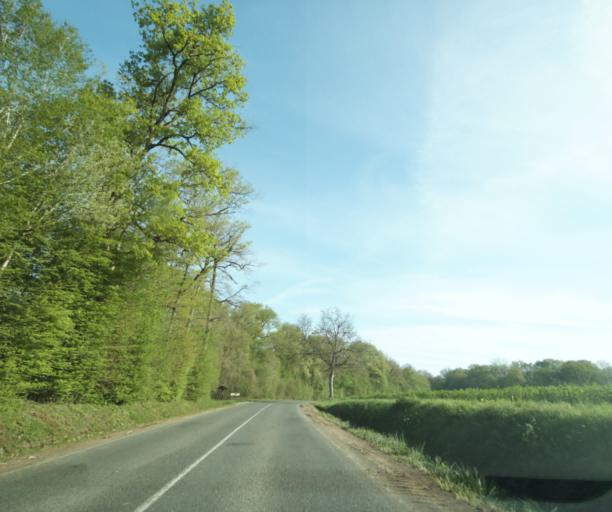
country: FR
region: Ile-de-France
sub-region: Departement de Seine-et-Marne
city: Vernou-la-Celle-sur-Seine
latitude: 48.4056
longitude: 2.8346
